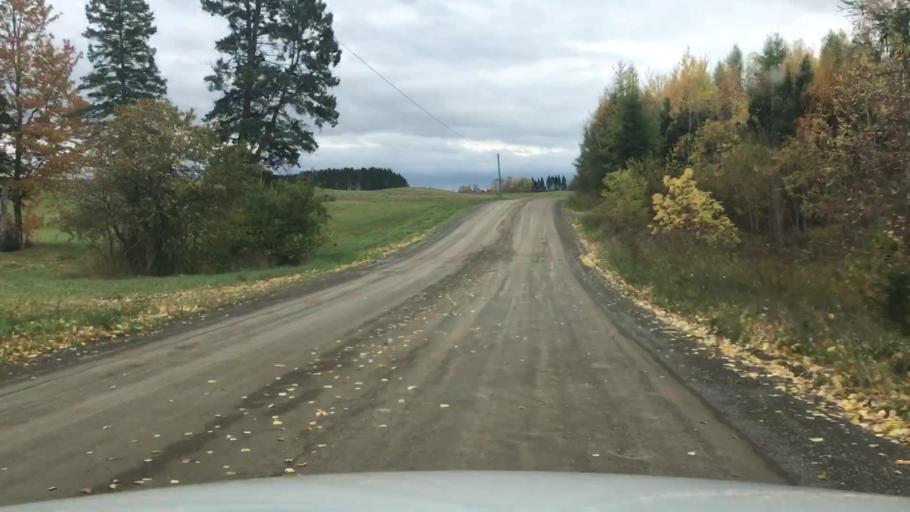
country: US
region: Maine
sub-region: Aroostook County
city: Easton
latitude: 46.5163
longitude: -67.8833
